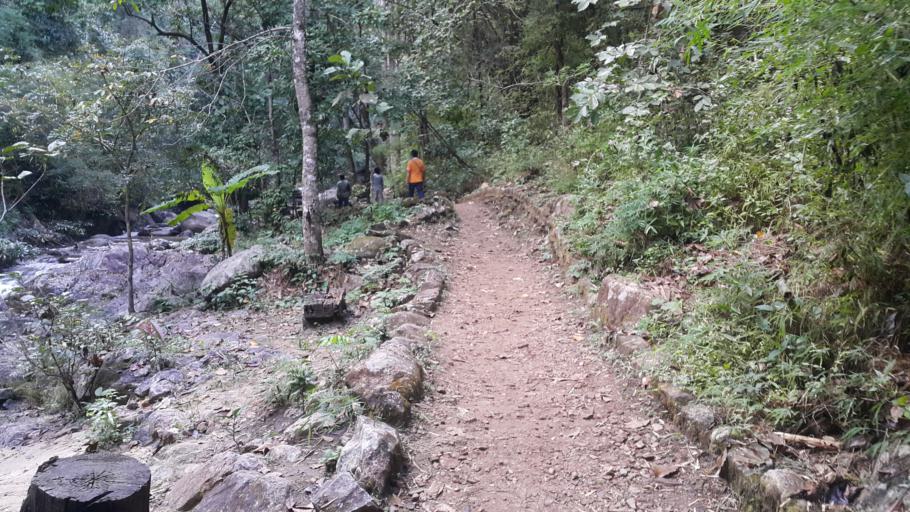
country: TH
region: Lampang
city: Mueang Pan
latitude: 18.8416
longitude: 99.4686
